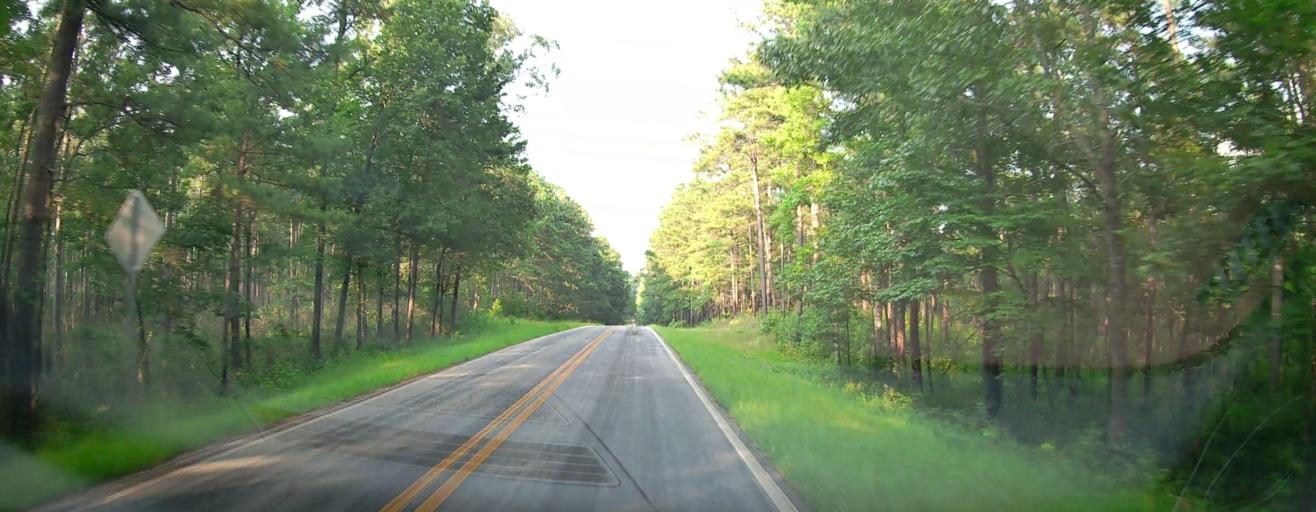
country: US
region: Georgia
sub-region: Jones County
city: Gray
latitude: 33.0977
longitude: -83.6792
